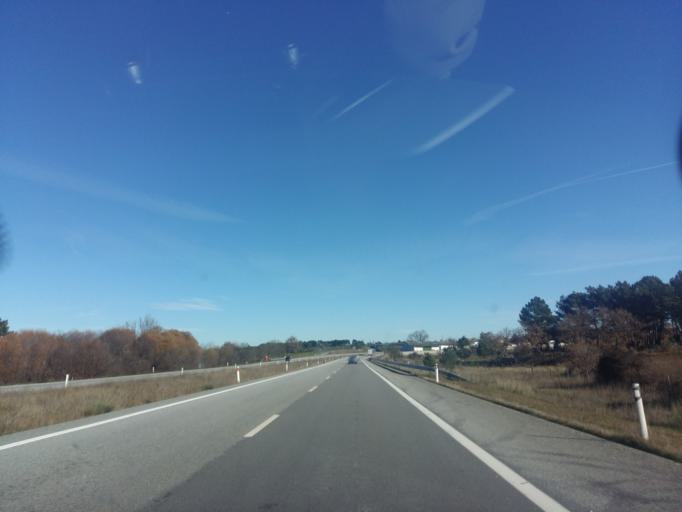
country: PT
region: Guarda
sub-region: Guarda
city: Sequeira
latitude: 40.6018
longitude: -7.1082
